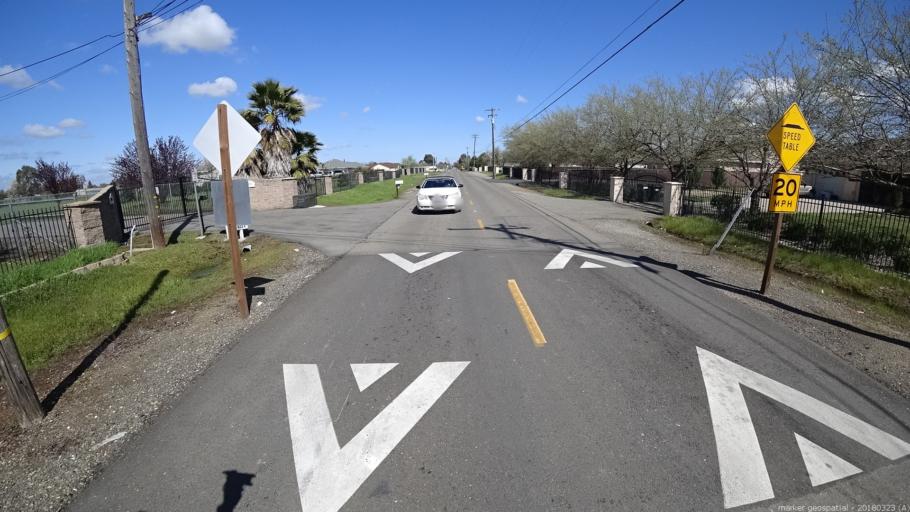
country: US
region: California
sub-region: Sacramento County
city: North Highlands
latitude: 38.6806
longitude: -121.4106
